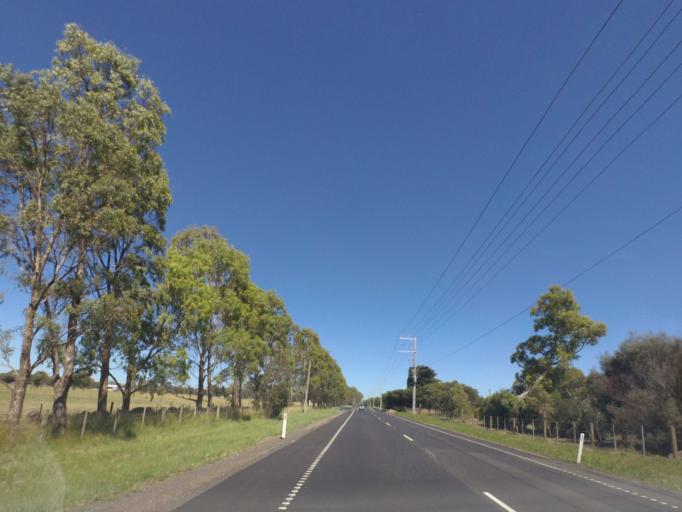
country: AU
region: Victoria
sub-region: Whittlesea
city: Mernda
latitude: -37.5523
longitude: 145.0607
